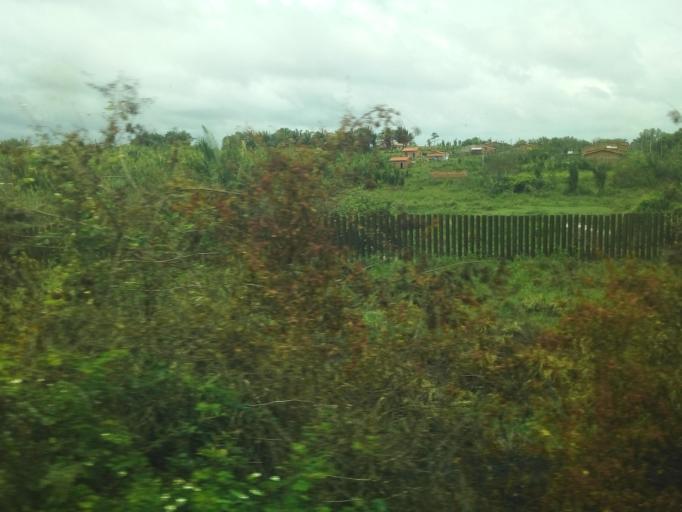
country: BR
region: Maranhao
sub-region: Vitoria Do Mearim
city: Vitoria do Mearim
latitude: -3.5870
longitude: -44.9669
